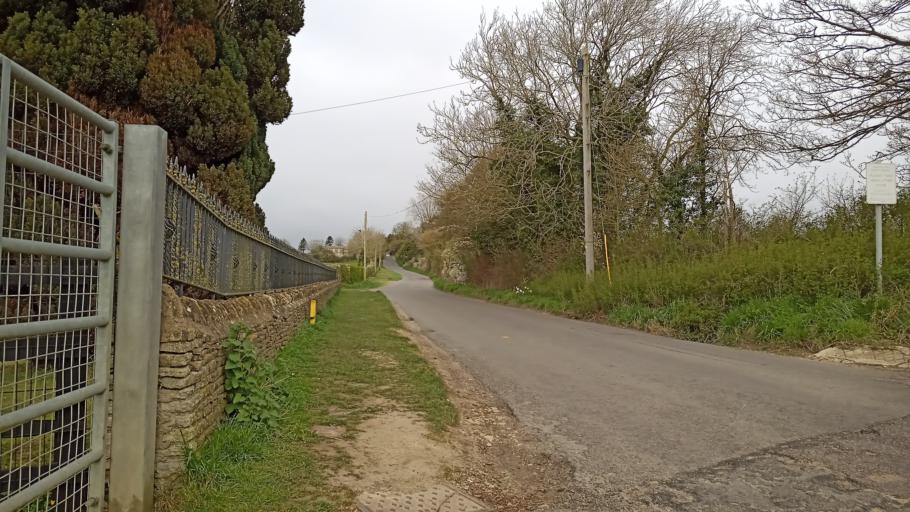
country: GB
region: England
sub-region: Oxfordshire
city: Witney
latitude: 51.7967
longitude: -1.4930
